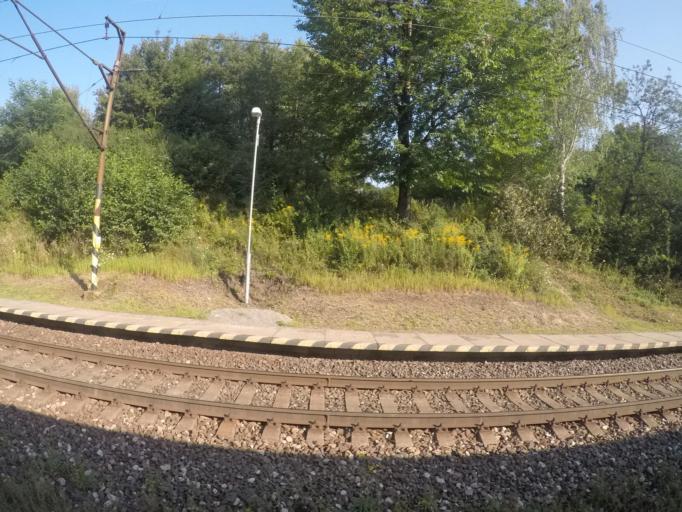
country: SK
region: Kosicky
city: Gelnica
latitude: 48.8745
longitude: 21.1083
